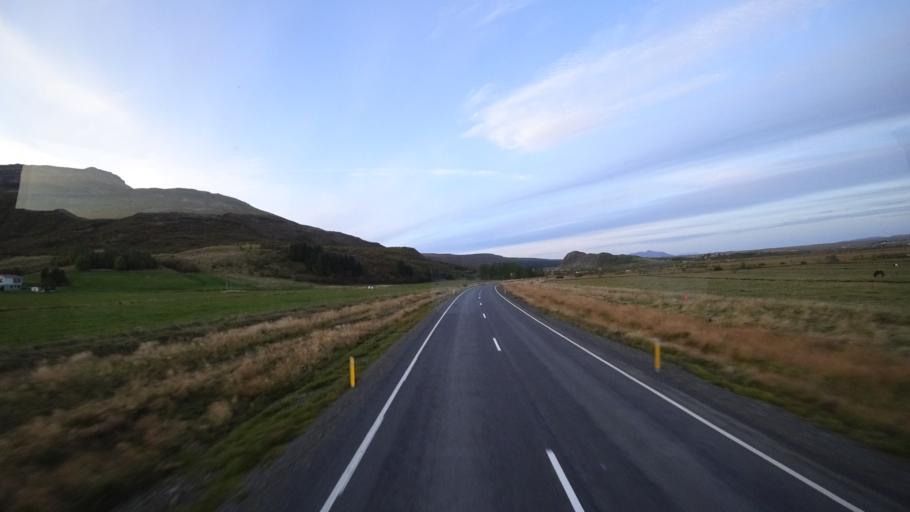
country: IS
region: South
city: Selfoss
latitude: 64.3012
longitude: -20.3305
